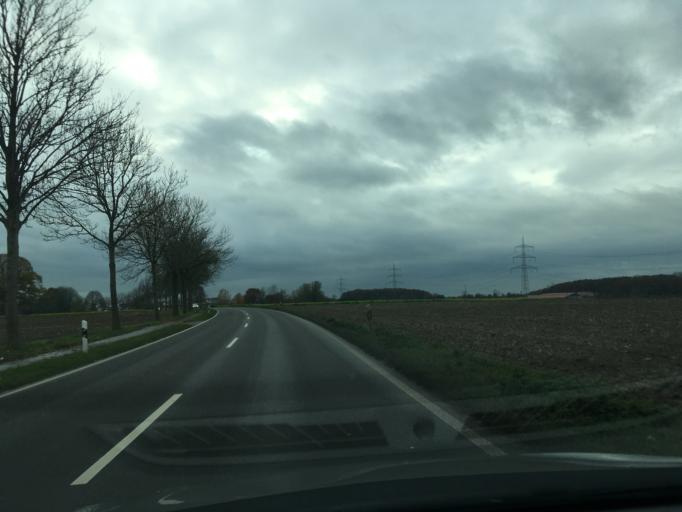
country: DE
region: North Rhine-Westphalia
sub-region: Regierungsbezirk Munster
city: Ahaus
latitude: 52.0924
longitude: 6.9655
